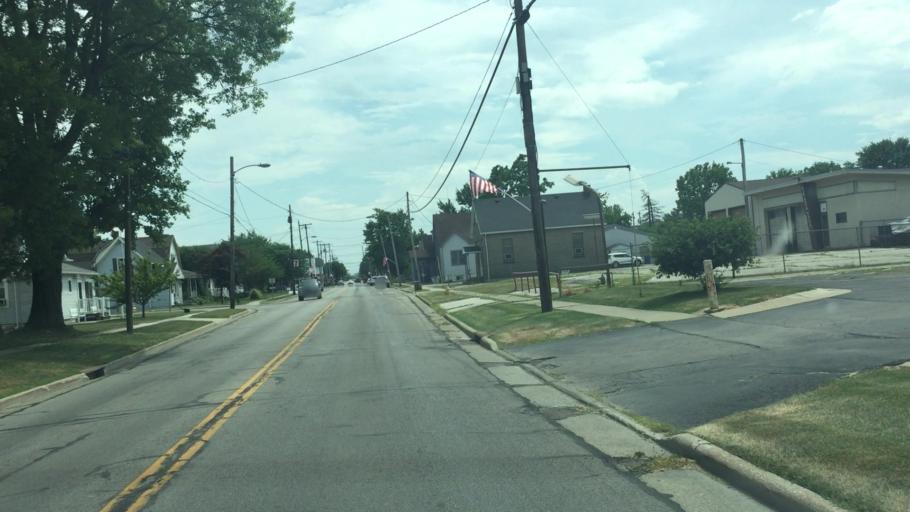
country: US
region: Ohio
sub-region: Wood County
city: Walbridge
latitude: 41.5905
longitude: -83.4934
